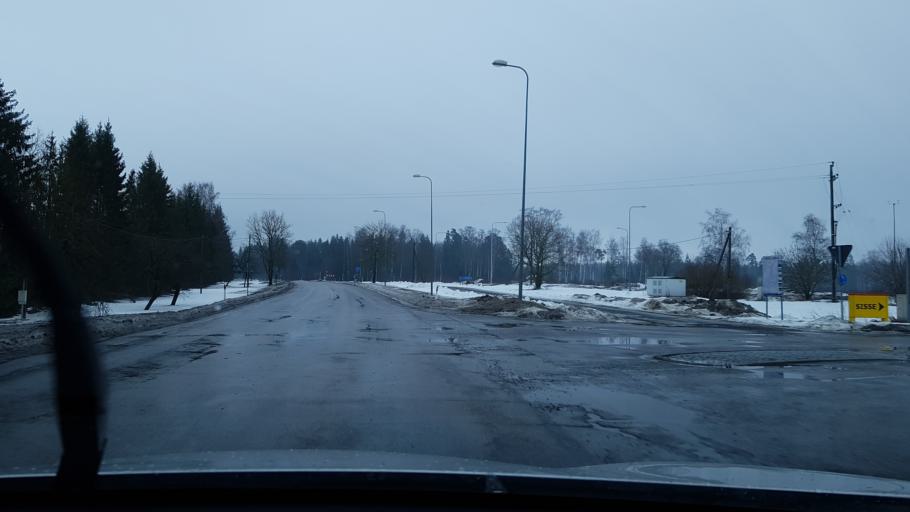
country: EE
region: Raplamaa
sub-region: Maerjamaa vald
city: Marjamaa
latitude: 58.9219
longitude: 24.4569
